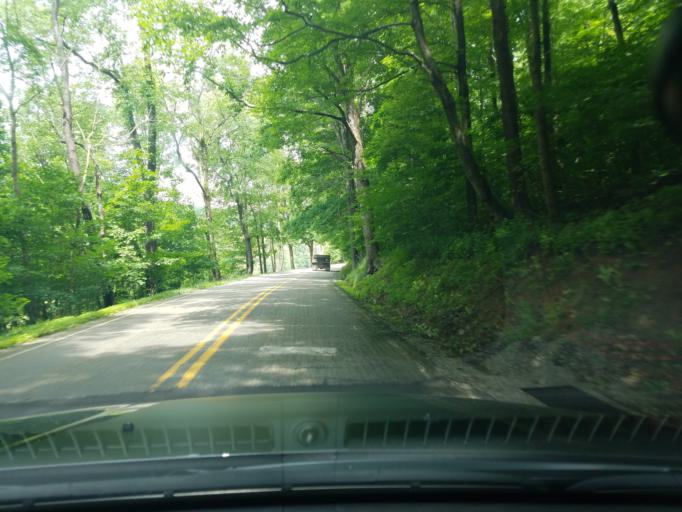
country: US
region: Pennsylvania
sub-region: Fayette County
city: Bear Rocks
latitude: 40.1682
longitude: -79.3623
